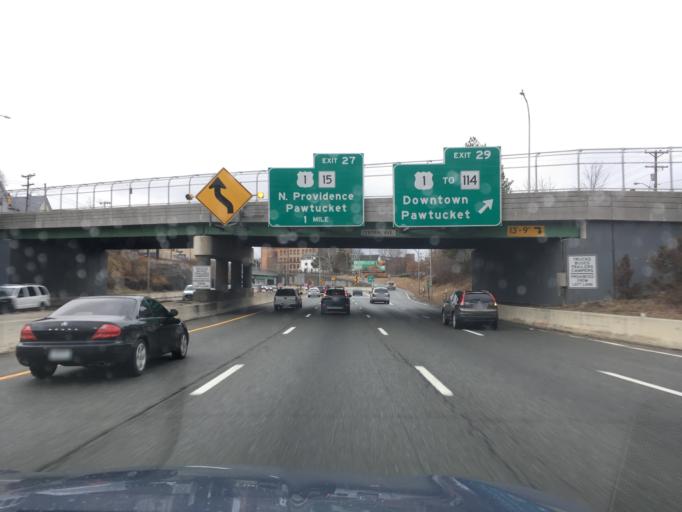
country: US
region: Rhode Island
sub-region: Providence County
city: Pawtucket
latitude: 41.8859
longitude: -71.3788
